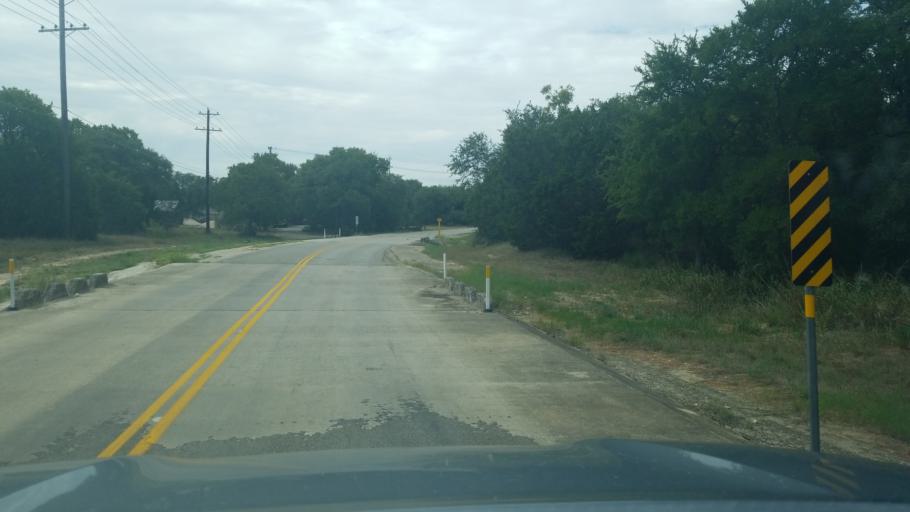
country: US
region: Texas
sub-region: Comal County
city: Bulverde
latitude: 29.7883
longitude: -98.4111
